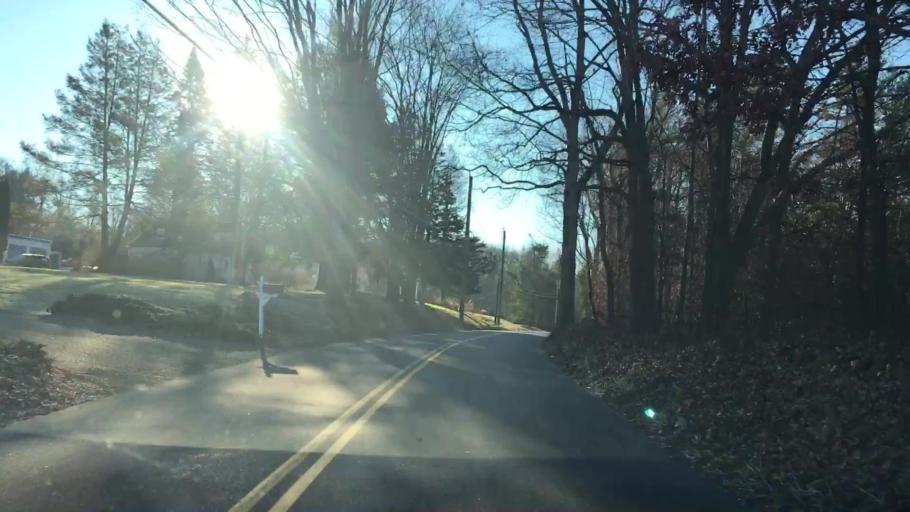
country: US
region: Connecticut
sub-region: New Haven County
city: Cheshire Village
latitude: 41.5525
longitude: -72.8687
